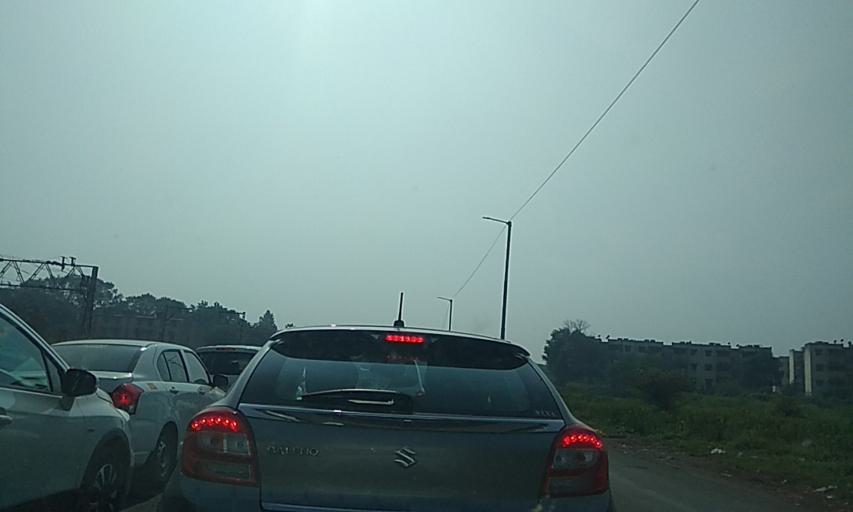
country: IN
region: Maharashtra
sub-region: Pune Division
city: Khadki
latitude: 18.5584
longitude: 73.8436
